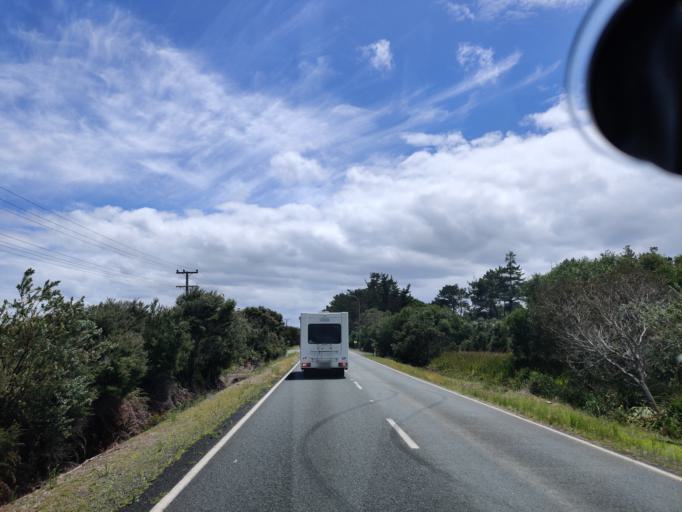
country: NZ
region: Northland
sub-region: Far North District
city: Kaitaia
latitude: -34.7423
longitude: 173.0466
